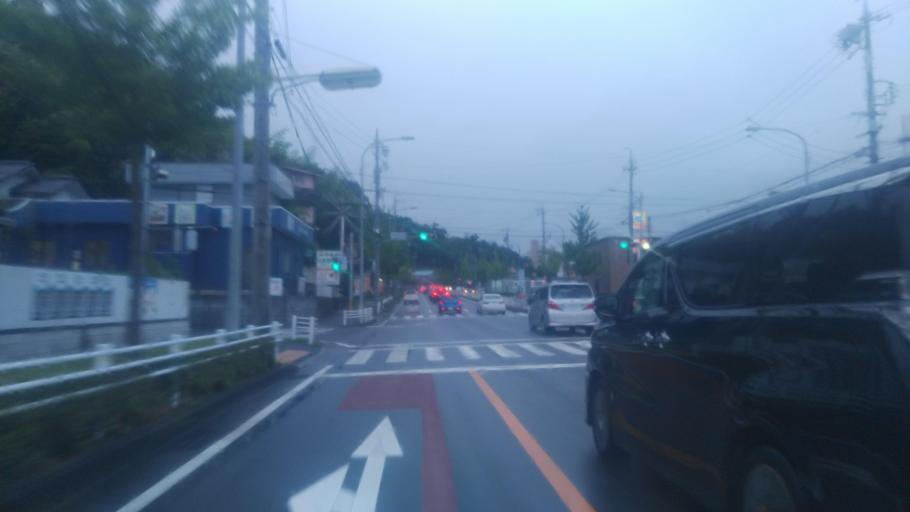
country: JP
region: Aichi
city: Kasugai
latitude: 35.2309
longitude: 136.9970
